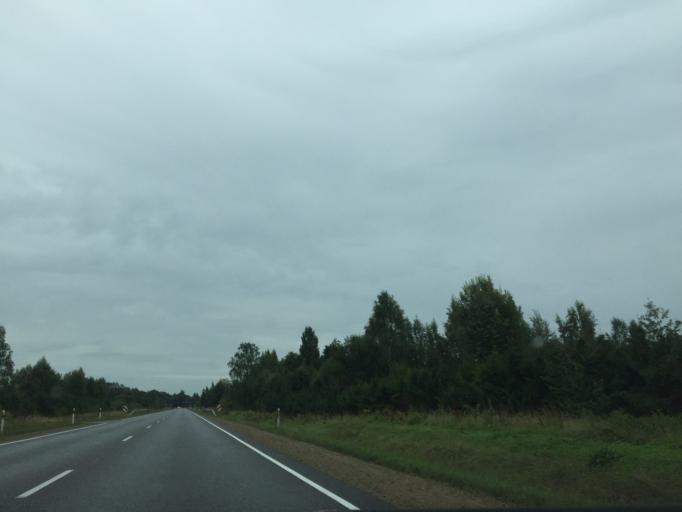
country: LV
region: Livani
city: Livani
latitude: 56.3941
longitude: 26.1447
